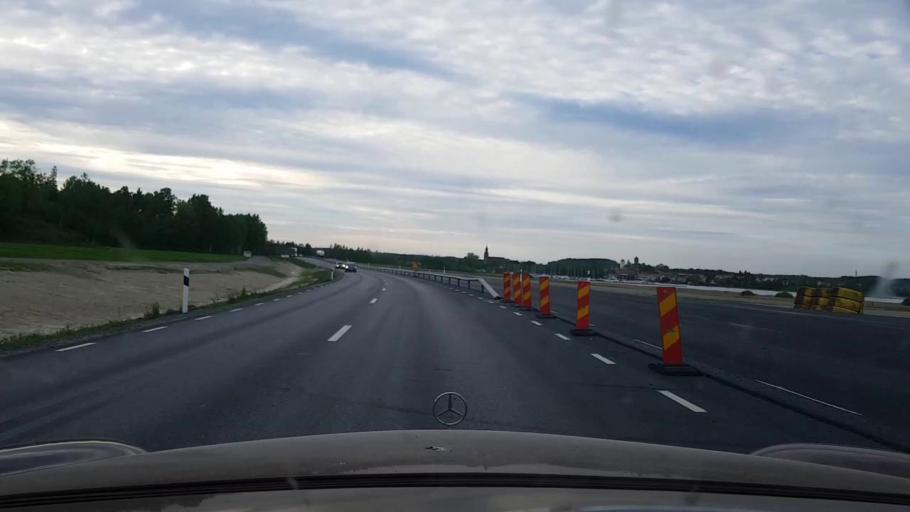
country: SE
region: OErebro
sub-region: Askersunds Kommun
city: Askersund
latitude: 58.8663
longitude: 14.9010
